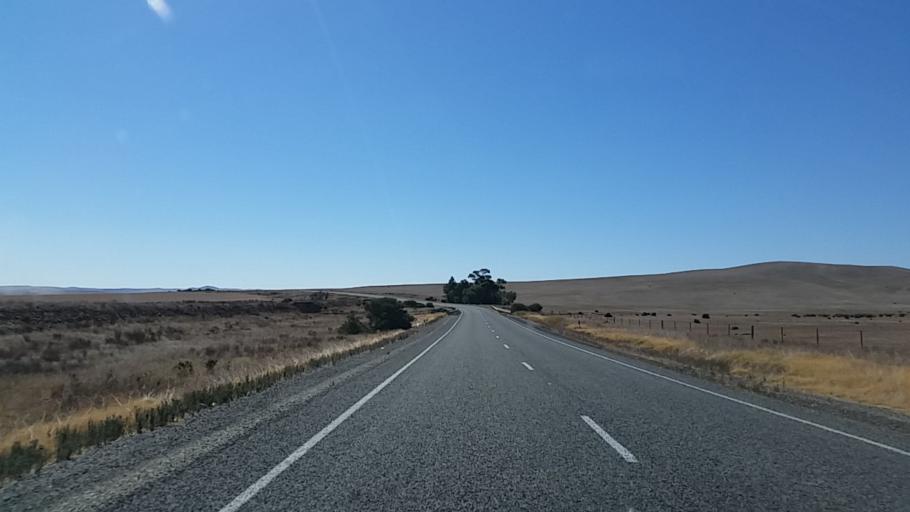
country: AU
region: South Australia
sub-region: Northern Areas
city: Jamestown
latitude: -33.3133
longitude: 138.8823
